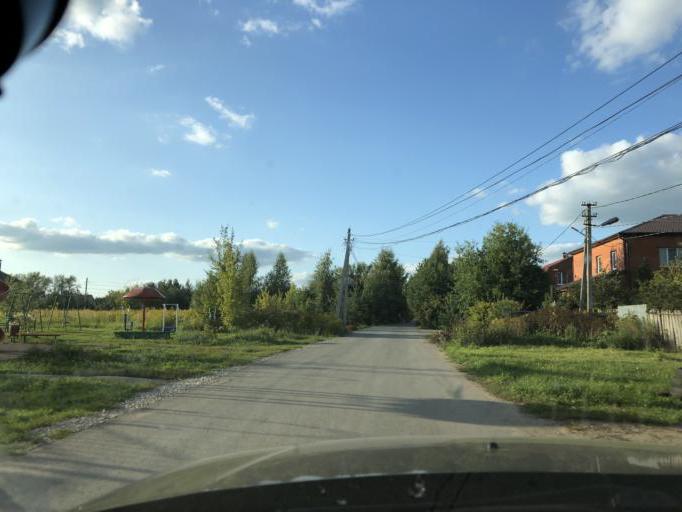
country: RU
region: Tula
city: Kosaya Gora
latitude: 54.1761
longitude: 37.5443
